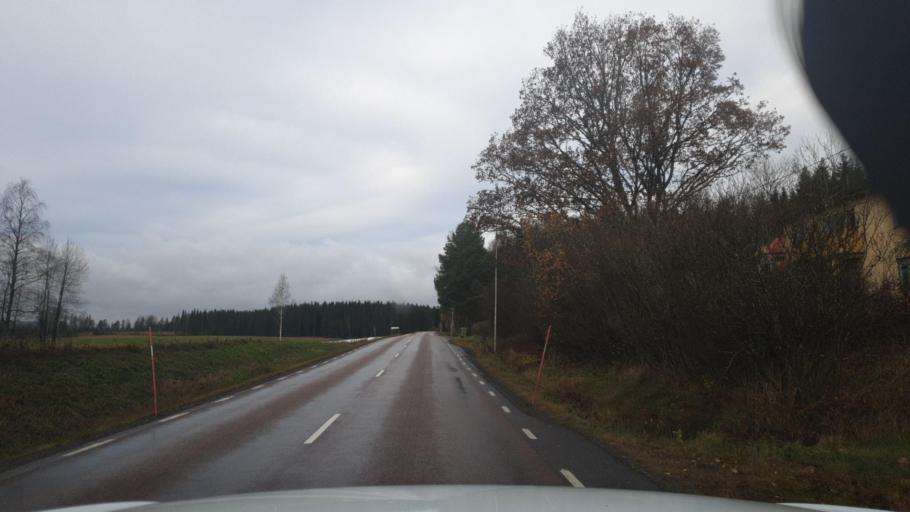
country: SE
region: Vaermland
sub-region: Eda Kommun
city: Charlottenberg
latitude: 59.8033
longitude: 12.2200
